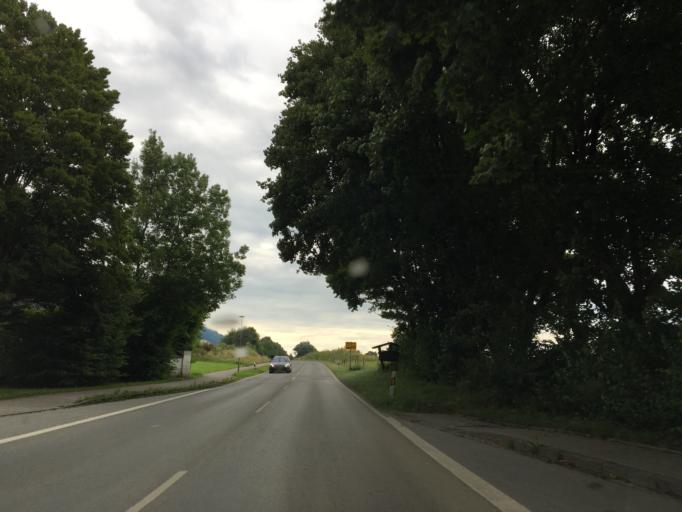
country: DE
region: Bavaria
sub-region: Upper Bavaria
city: Flintsbach
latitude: 47.7267
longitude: 12.1195
